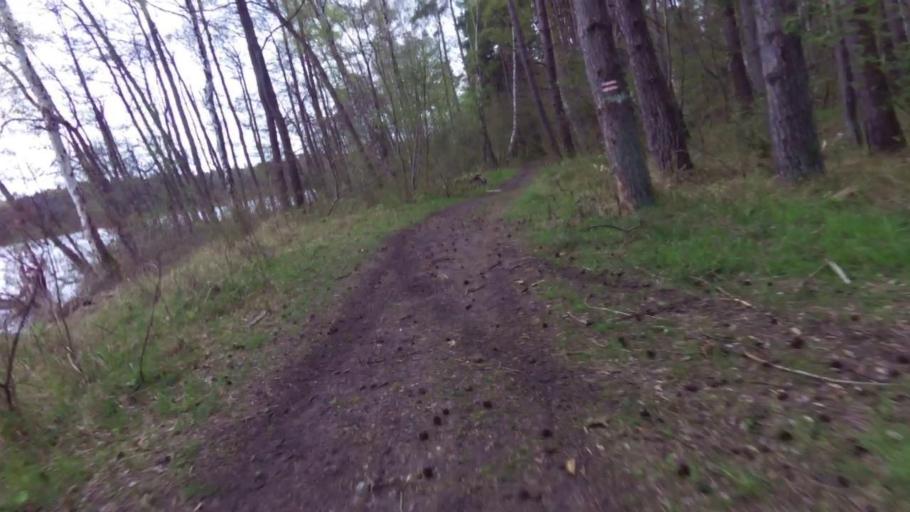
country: PL
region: West Pomeranian Voivodeship
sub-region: Powiat kamienski
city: Dziwnow
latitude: 54.0170
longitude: 14.7197
